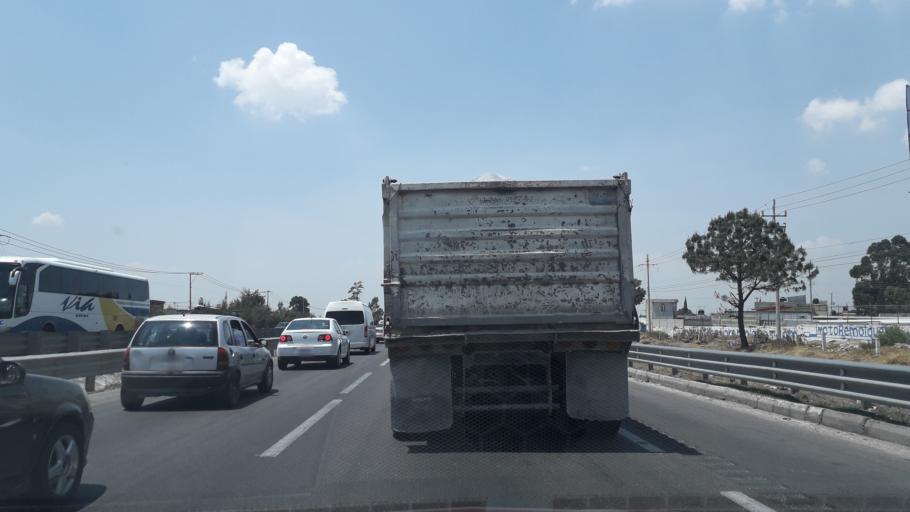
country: MX
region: Puebla
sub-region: Amozoc
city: Casa Blanca
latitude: 19.0684
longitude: -98.1232
